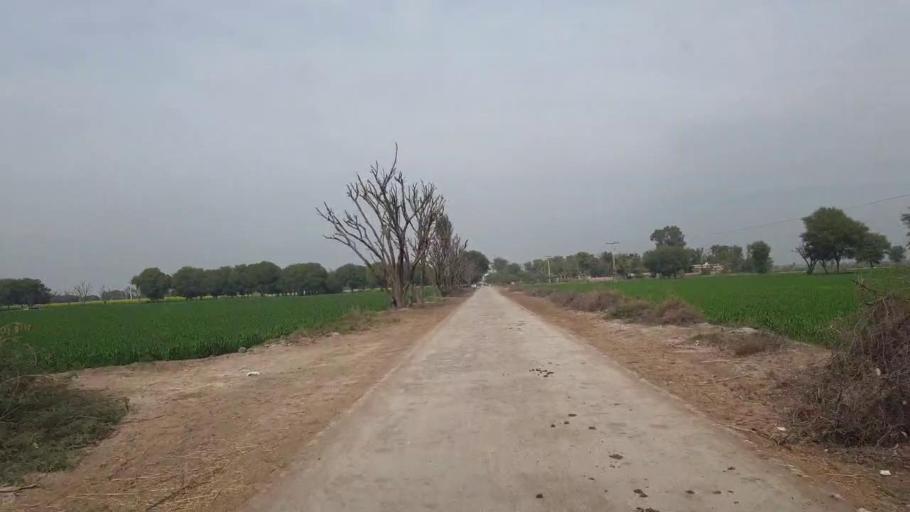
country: PK
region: Sindh
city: Nawabshah
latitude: 26.1205
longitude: 68.4800
